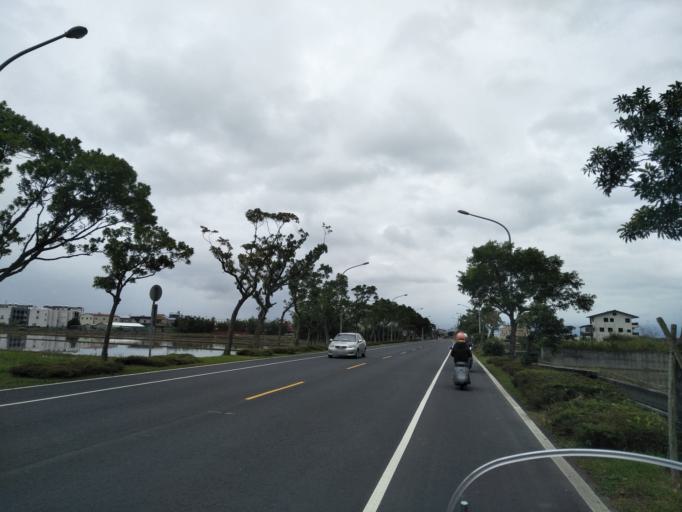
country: TW
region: Taiwan
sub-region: Yilan
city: Yilan
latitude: 24.7794
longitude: 121.7832
